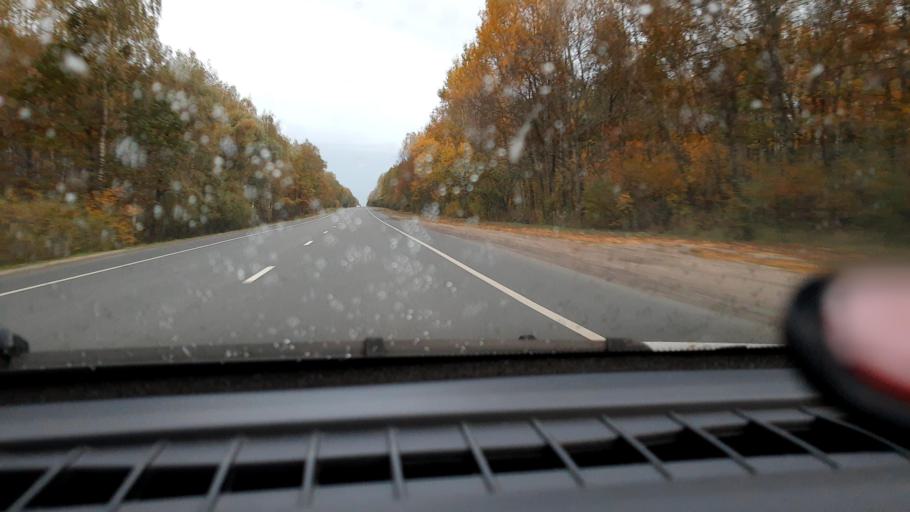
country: RU
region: Vladimir
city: Orgtrud
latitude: 56.2045
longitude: 40.7364
